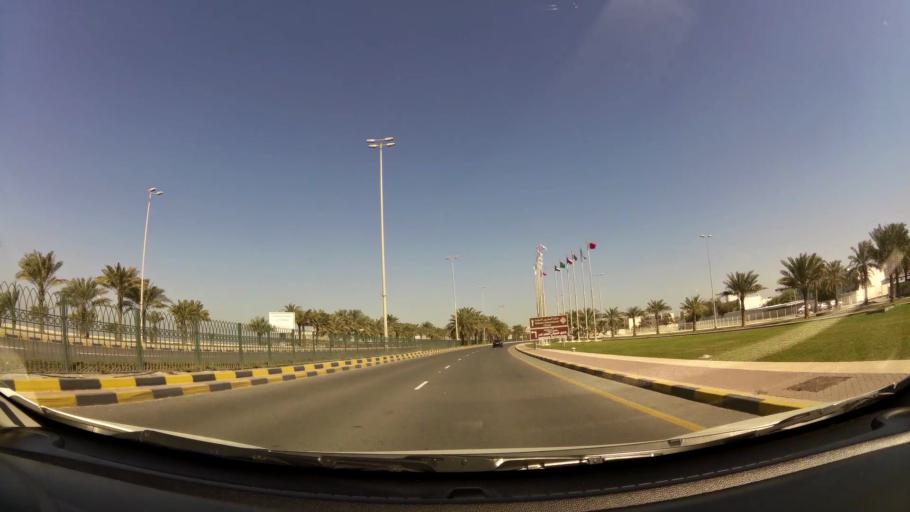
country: BH
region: Muharraq
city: Al Muharraq
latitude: 26.2539
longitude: 50.6037
